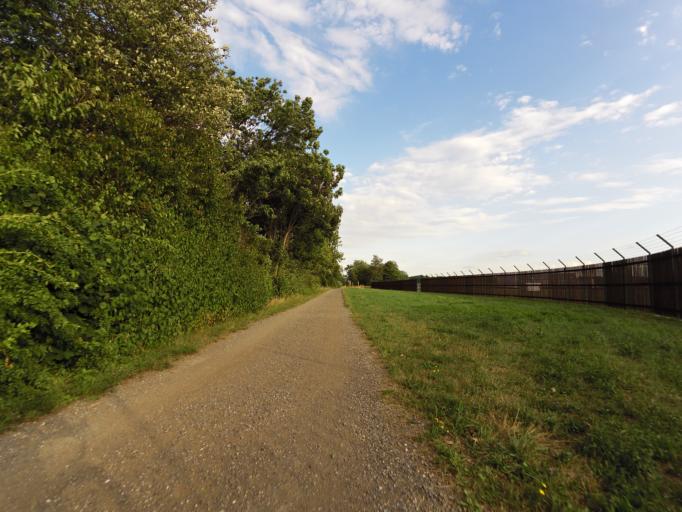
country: CH
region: Zurich
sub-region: Bezirk Buelach
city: Kloten / Freienberg (Chanzler-Chlini Chaseren)
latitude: 47.4612
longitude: 8.5678
